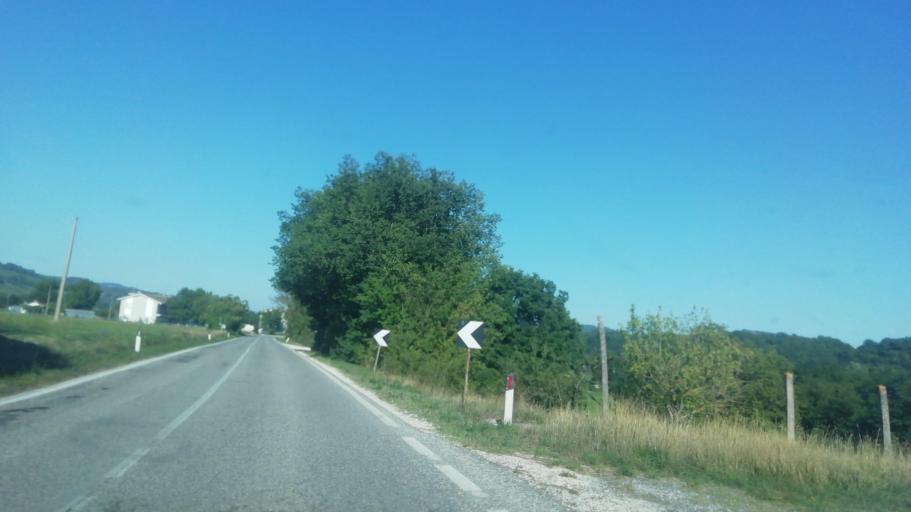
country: IT
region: The Marches
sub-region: Provincia di Pesaro e Urbino
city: Pergola
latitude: 43.5539
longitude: 12.8121
